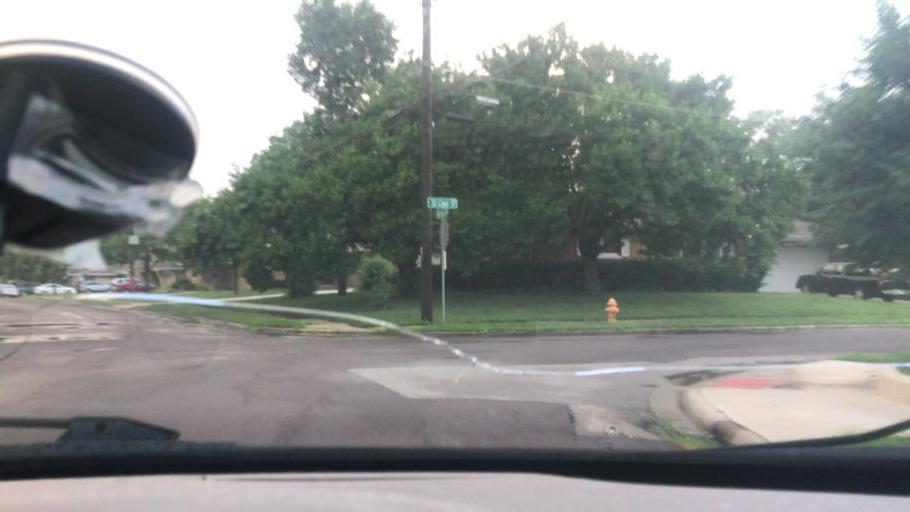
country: US
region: Illinois
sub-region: Tazewell County
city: Pekin
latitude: 40.5491
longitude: -89.6129
